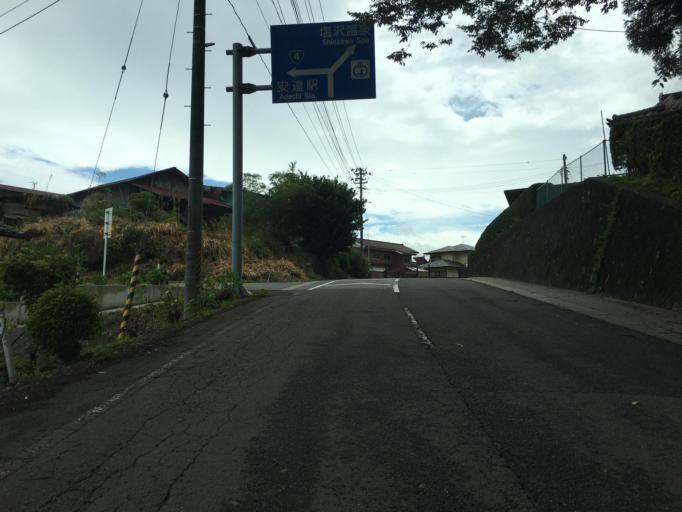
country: JP
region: Fukushima
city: Nihommatsu
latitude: 37.6259
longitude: 140.4574
